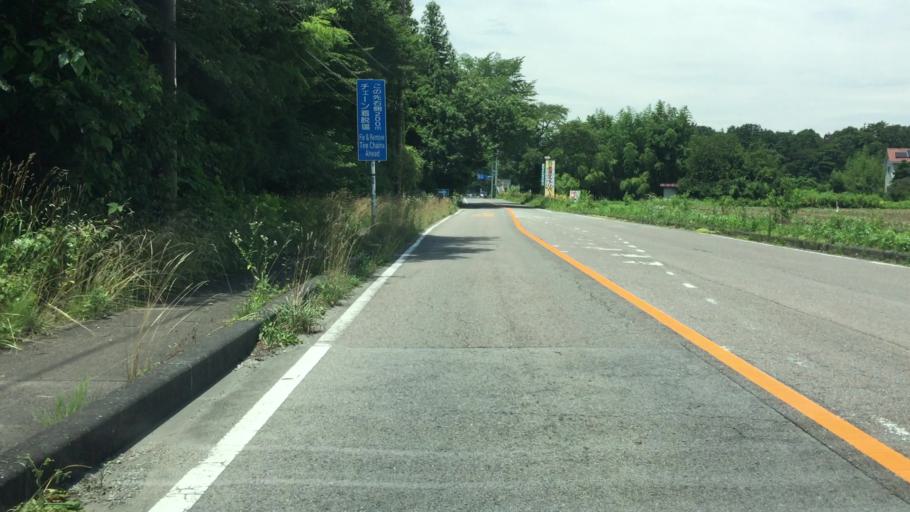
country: JP
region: Tochigi
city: Kuroiso
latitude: 37.0133
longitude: 139.9619
